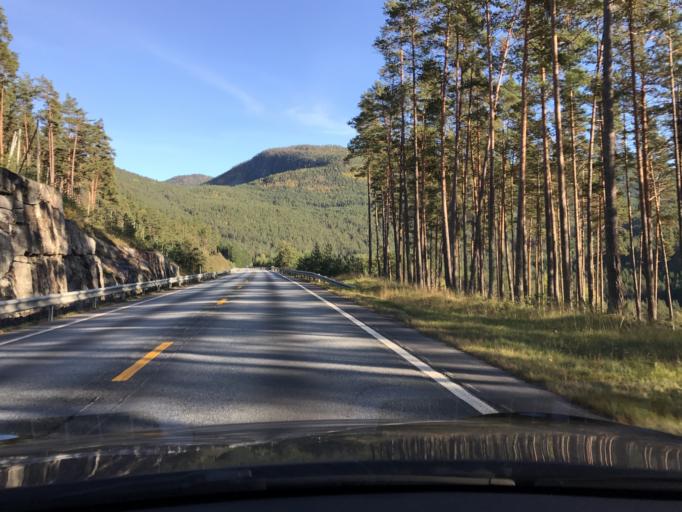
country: NO
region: Sogn og Fjordane
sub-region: Sogndal
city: Sogndalsfjora
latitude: 61.1816
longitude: 7.2826
